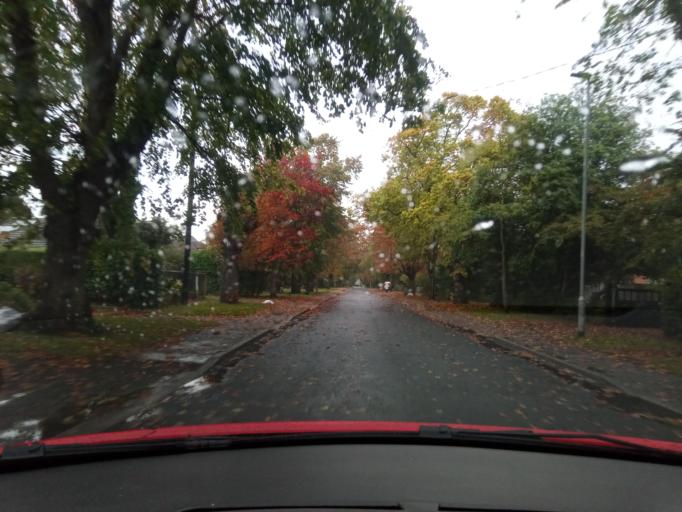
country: GB
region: England
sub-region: Essex
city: West Mersea
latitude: 51.7779
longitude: 0.9278
